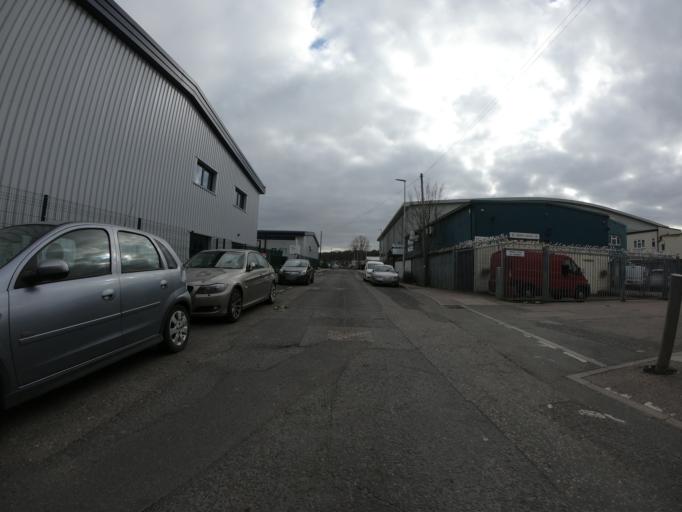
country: GB
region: England
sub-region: Greater London
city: Belvedere
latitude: 51.4964
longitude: 0.1614
